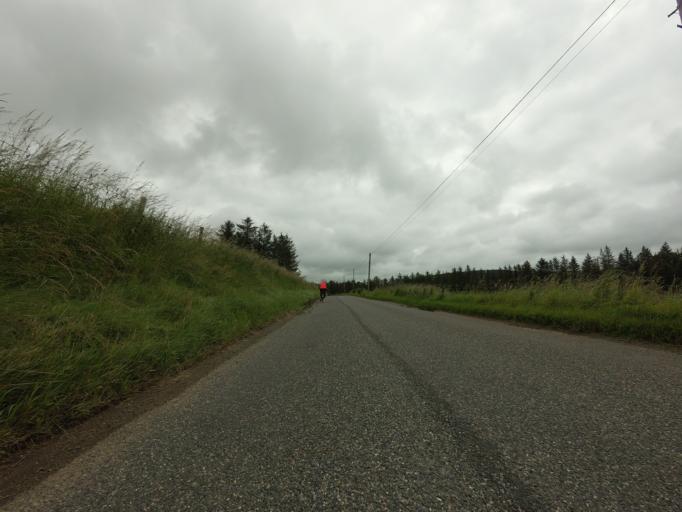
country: GB
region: Scotland
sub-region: Aberdeenshire
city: Turriff
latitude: 57.5337
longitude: -2.3786
